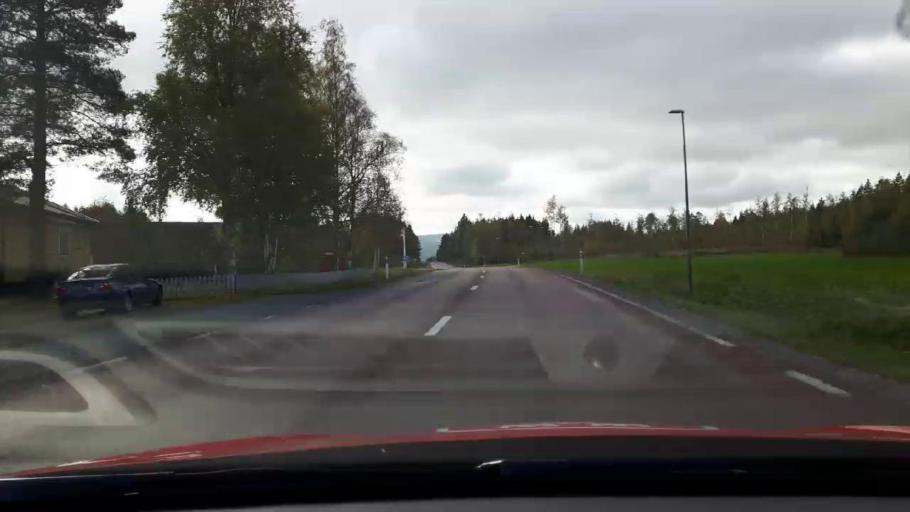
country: SE
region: Gaevleborg
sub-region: Ljusdals Kommun
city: Jaervsoe
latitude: 61.6894
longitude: 16.1499
